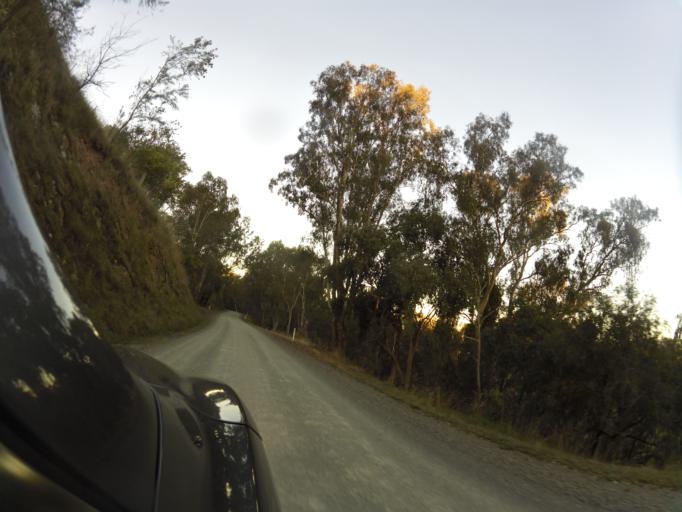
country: AU
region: Victoria
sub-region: Murrindindi
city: Alexandra
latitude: -37.1536
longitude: 145.5368
